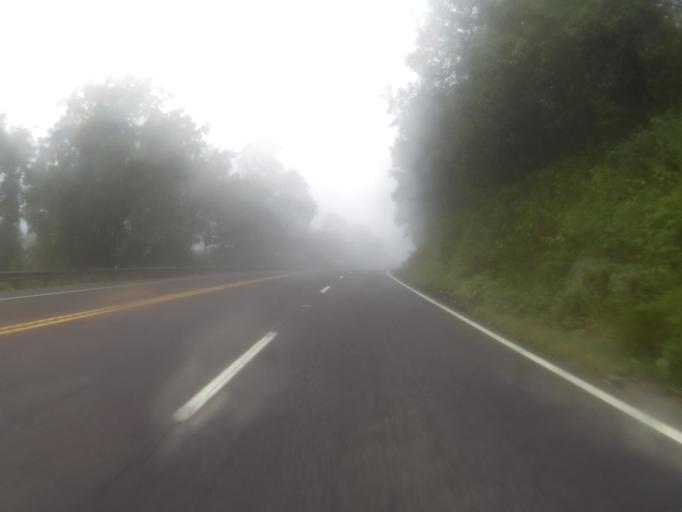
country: US
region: Virginia
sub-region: Page County
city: Luray
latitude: 38.6623
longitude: -78.3135
